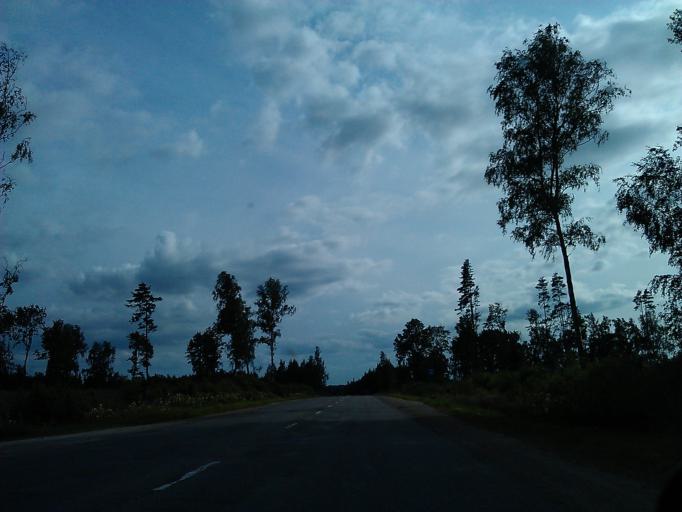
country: LV
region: Amatas Novads
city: Drabesi
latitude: 57.2715
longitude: 25.2776
